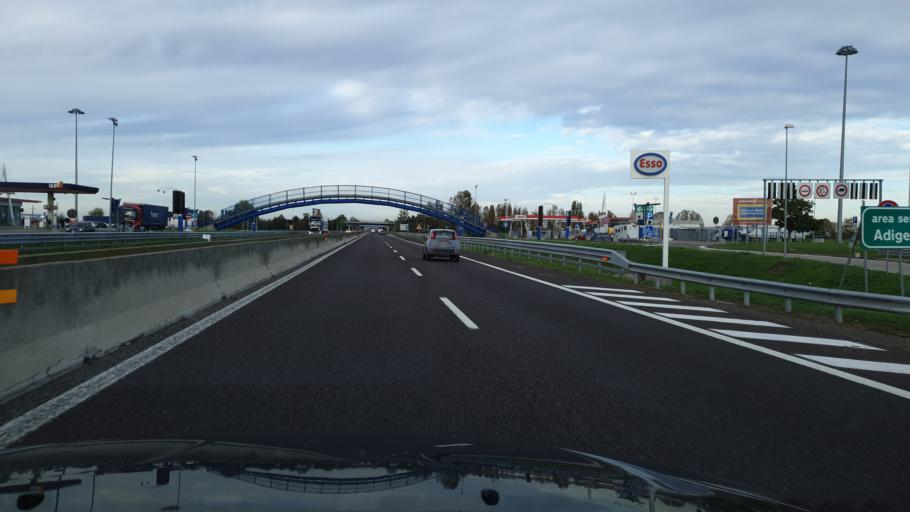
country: IT
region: Veneto
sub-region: Provincia di Rovigo
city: Costa di Rovigo
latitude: 45.0404
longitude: 11.7093
